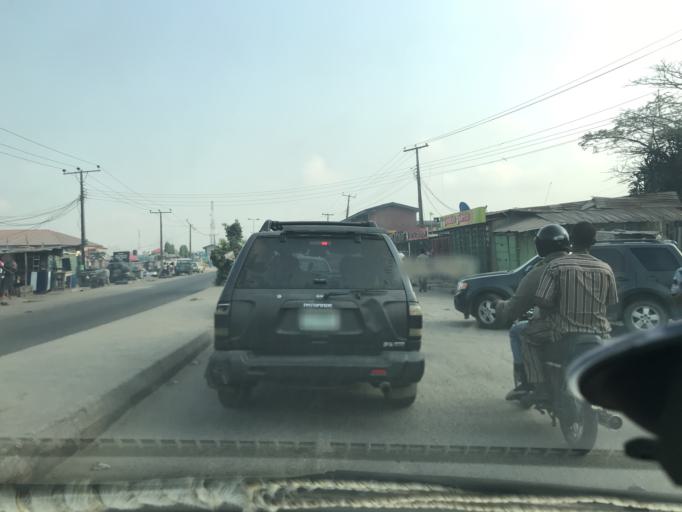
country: NG
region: Lagos
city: Ebute Ikorodu
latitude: 6.4889
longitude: 3.5806
